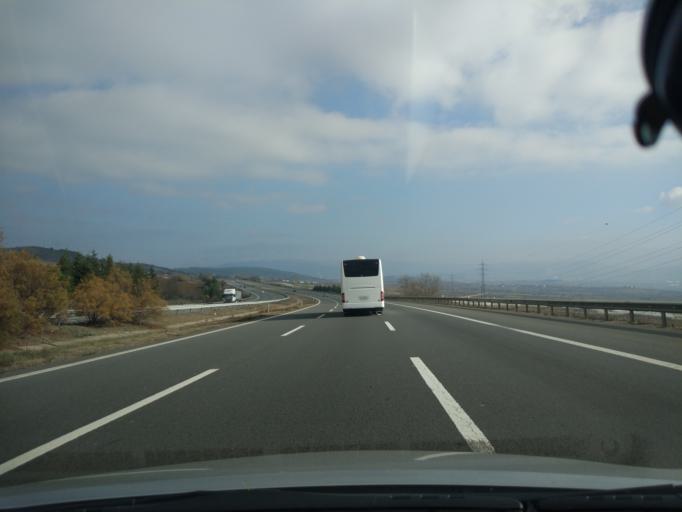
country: TR
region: Bolu
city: Bolu
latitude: 40.7709
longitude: 31.6714
